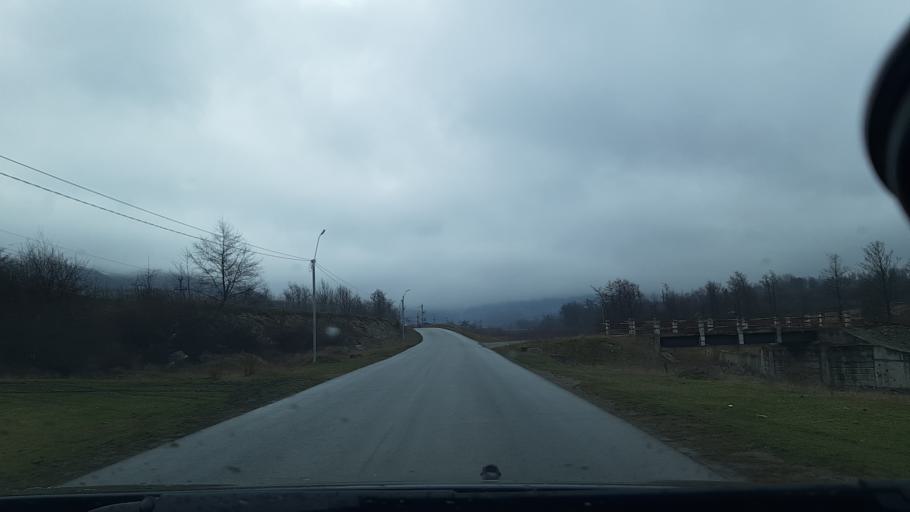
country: RO
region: Hunedoara
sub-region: Oras Petrila
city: Petrila
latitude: 45.4359
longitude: 23.4175
